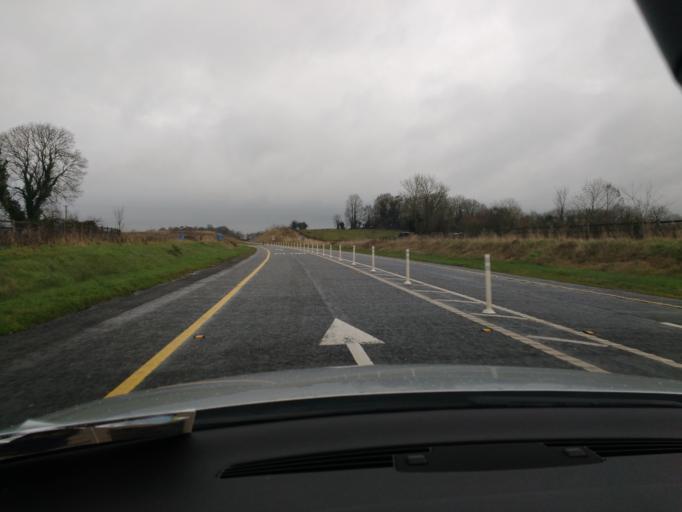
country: IE
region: Munster
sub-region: North Tipperary
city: Nenagh
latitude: 52.8489
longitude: -8.1552
